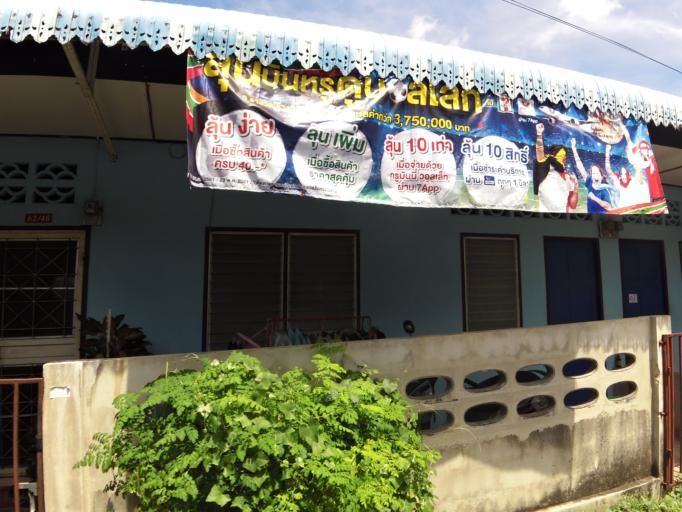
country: TH
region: Phuket
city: Ban Chalong
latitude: 7.8268
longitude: 98.3392
